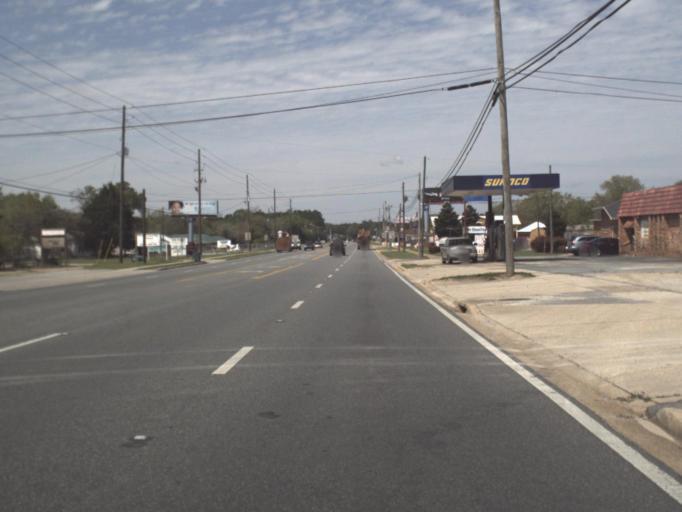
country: US
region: Florida
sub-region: Okaloosa County
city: Crestview
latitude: 30.7652
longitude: -86.5898
